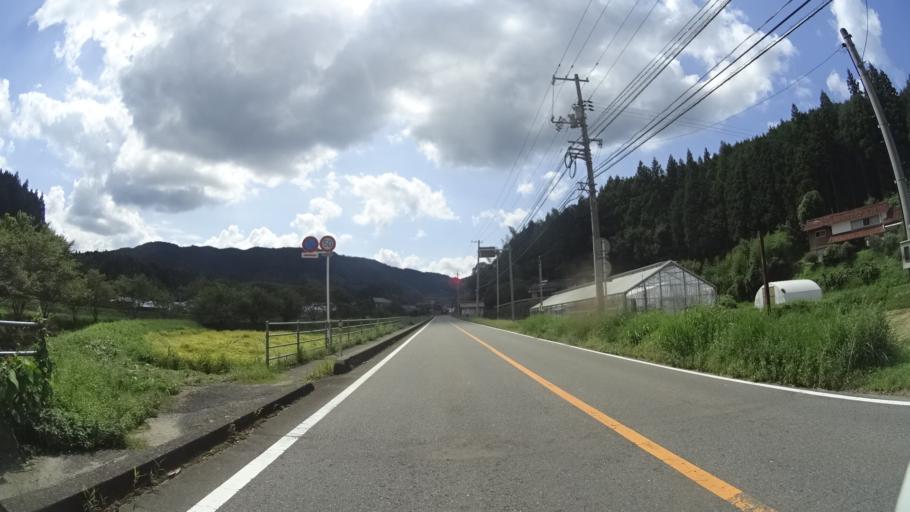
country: JP
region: Yamaguchi
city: Hagi
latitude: 34.4344
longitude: 131.4779
